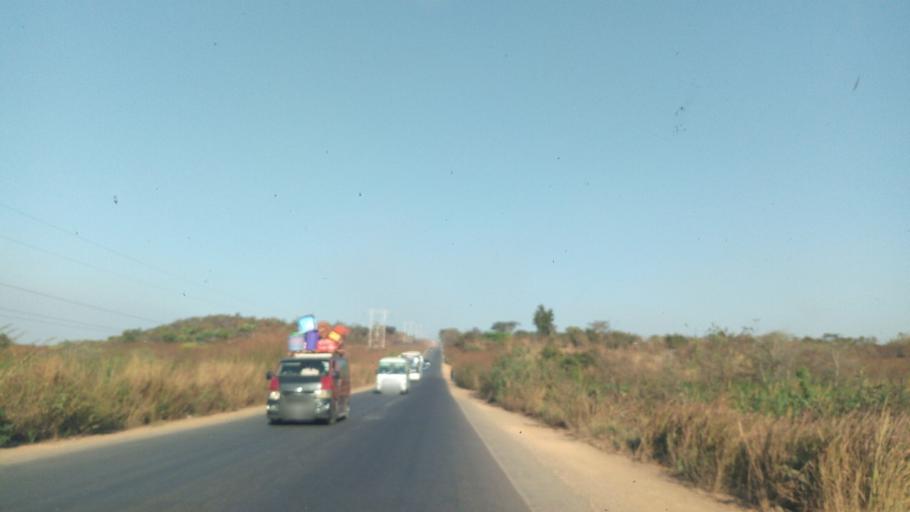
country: CD
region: Katanga
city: Likasi
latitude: -11.0543
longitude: 26.9627
